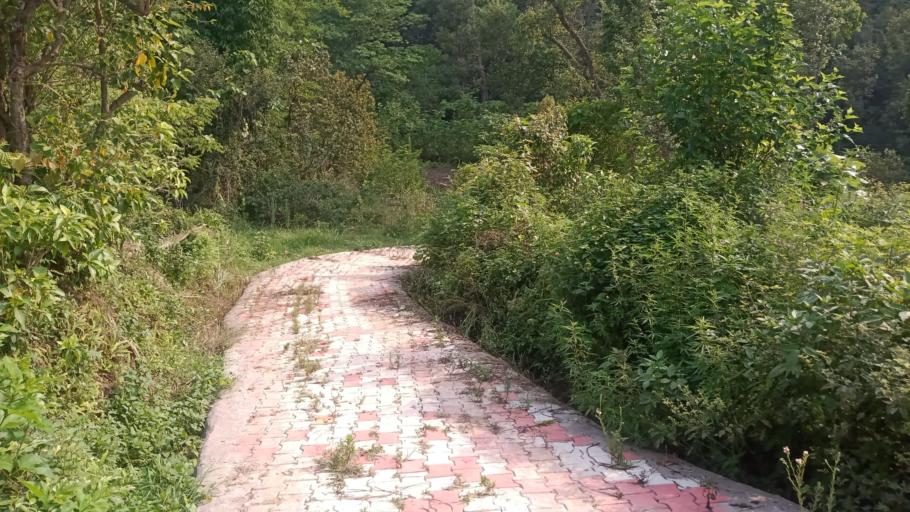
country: IN
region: Himachal Pradesh
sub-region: Hamirpur
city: Nadaun
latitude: 31.6957
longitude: 76.3013
